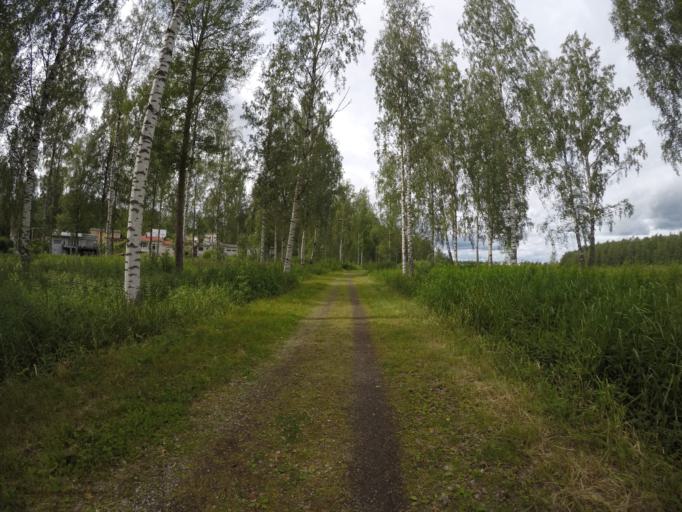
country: FI
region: Haeme
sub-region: Haemeenlinna
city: Haemeenlinna
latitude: 60.9833
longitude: 24.4805
